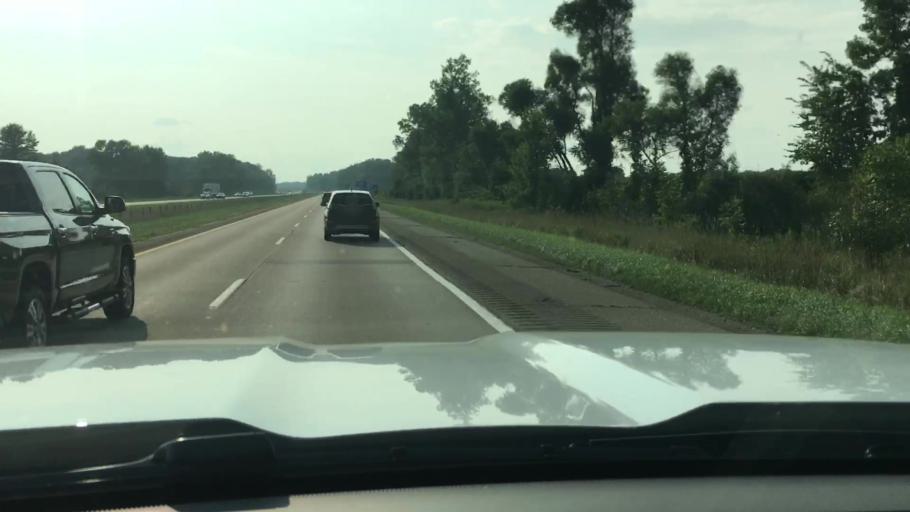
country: US
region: Michigan
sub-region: Kent County
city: Lowell
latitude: 42.8779
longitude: -85.3517
